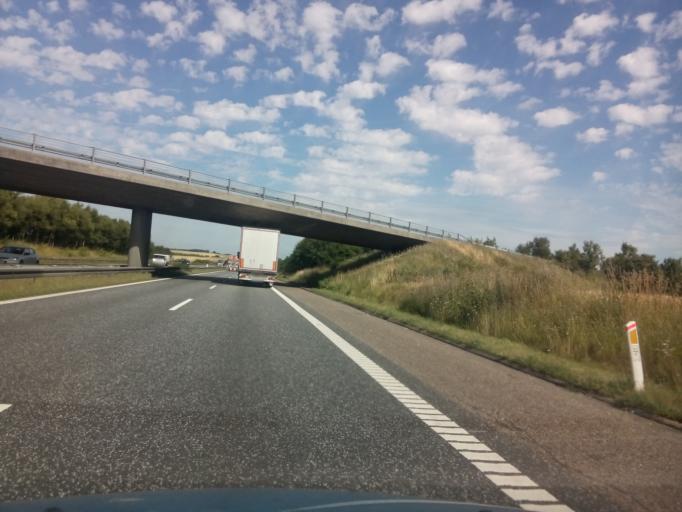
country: DK
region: Central Jutland
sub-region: Favrskov Kommune
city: Hadsten
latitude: 56.3410
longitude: 10.1219
